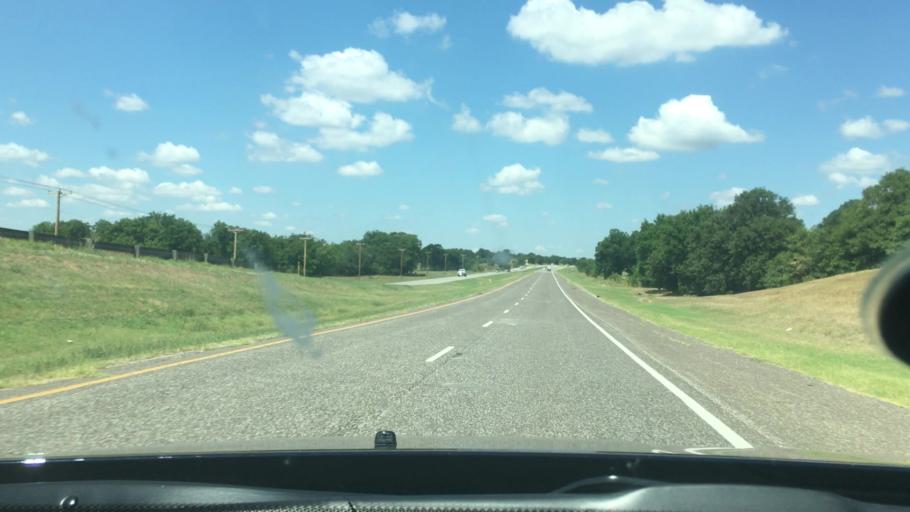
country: US
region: Oklahoma
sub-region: Carter County
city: Wilson
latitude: 34.1730
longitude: -97.3528
